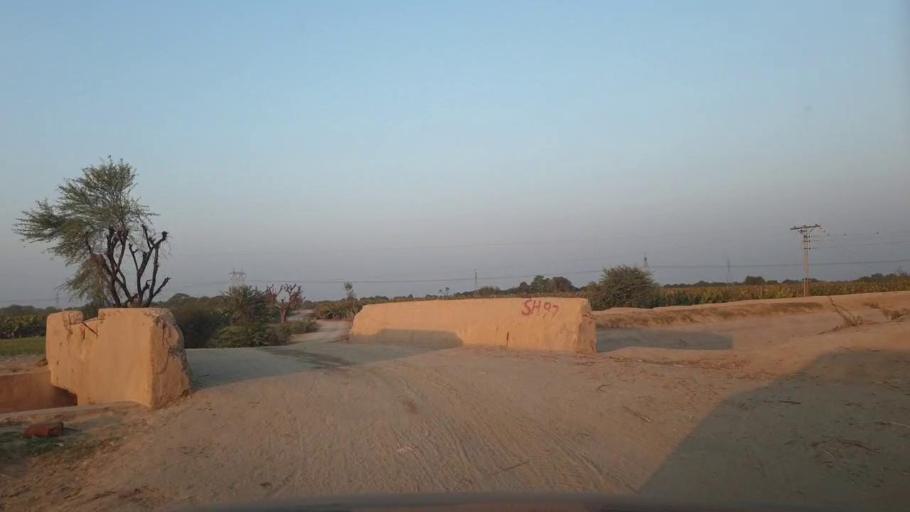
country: PK
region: Sindh
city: Bhit Shah
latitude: 25.8163
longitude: 68.5029
